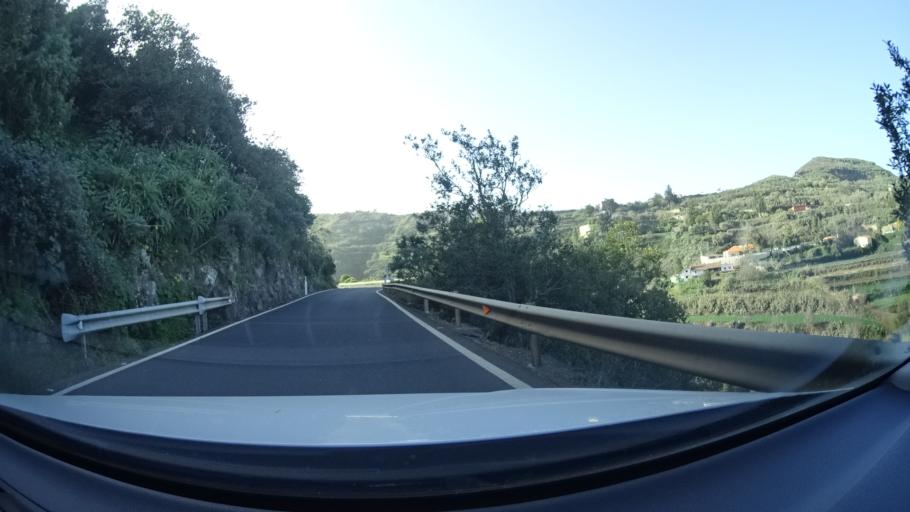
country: ES
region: Canary Islands
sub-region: Provincia de Las Palmas
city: Vega de San Mateo
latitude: 28.0261
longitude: -15.5506
